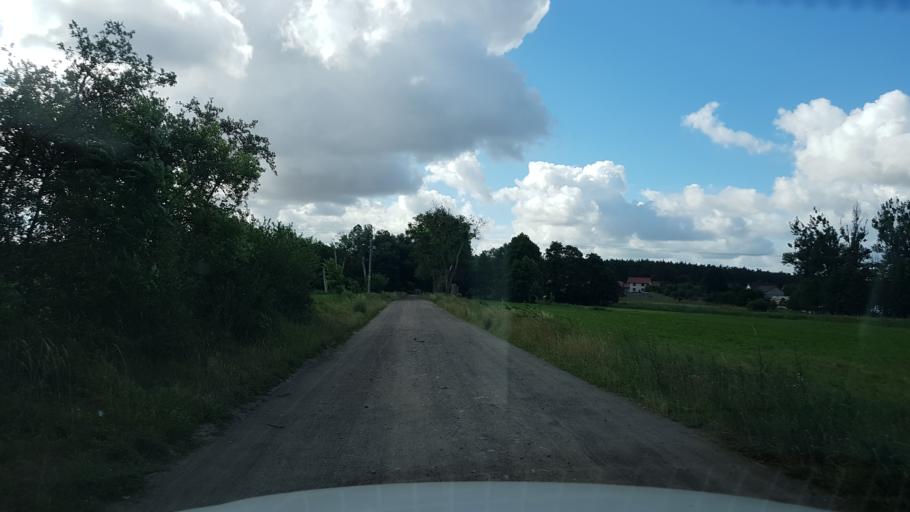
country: PL
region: West Pomeranian Voivodeship
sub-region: Powiat mysliborski
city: Debno
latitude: 52.7156
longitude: 14.6550
